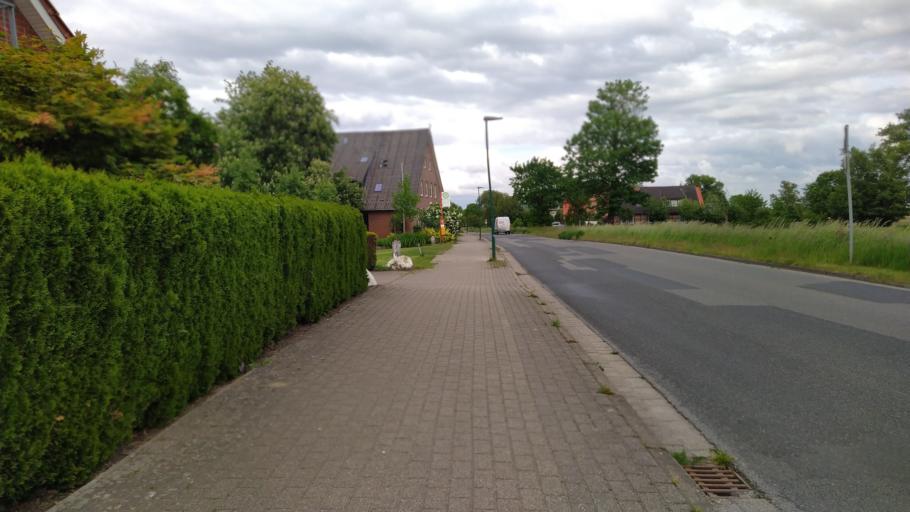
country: DE
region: Lower Saxony
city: Neu Wulmstorf
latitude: 53.4905
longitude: 9.7694
